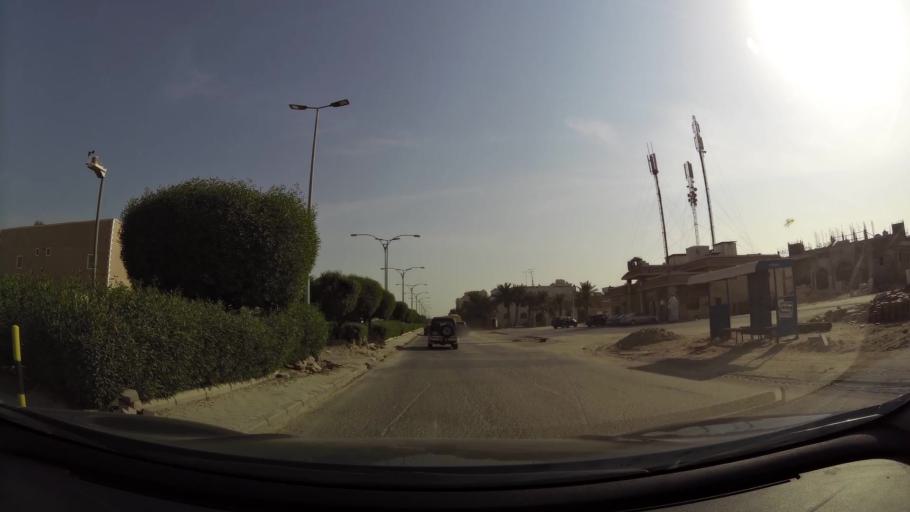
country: KW
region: Al Ahmadi
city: Ar Riqqah
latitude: 29.1474
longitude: 48.1061
